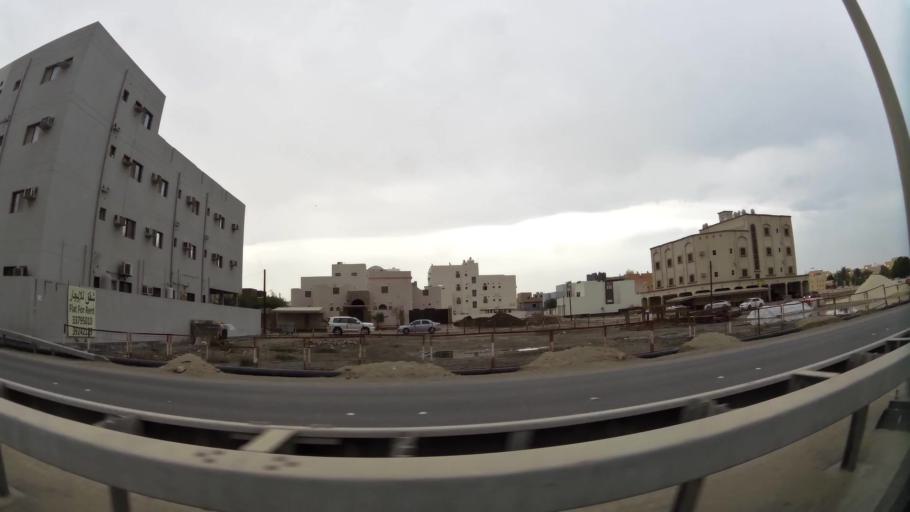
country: BH
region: Central Governorate
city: Madinat Hamad
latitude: 26.0945
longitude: 50.4904
